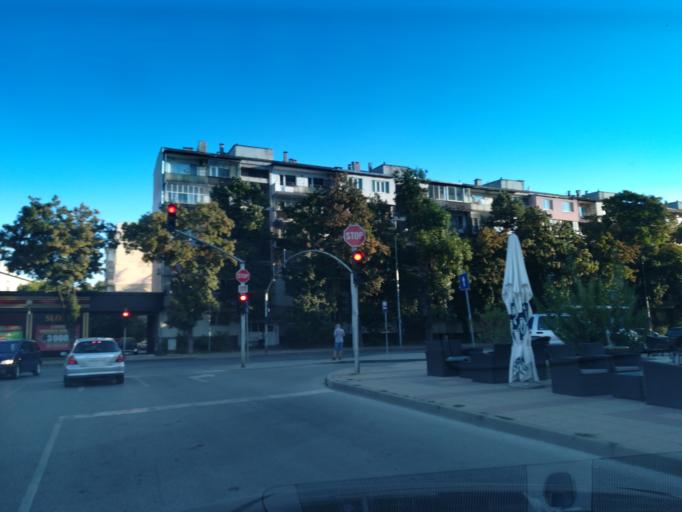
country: BG
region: Plovdiv
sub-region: Obshtina Plovdiv
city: Plovdiv
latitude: 42.1388
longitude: 24.7227
